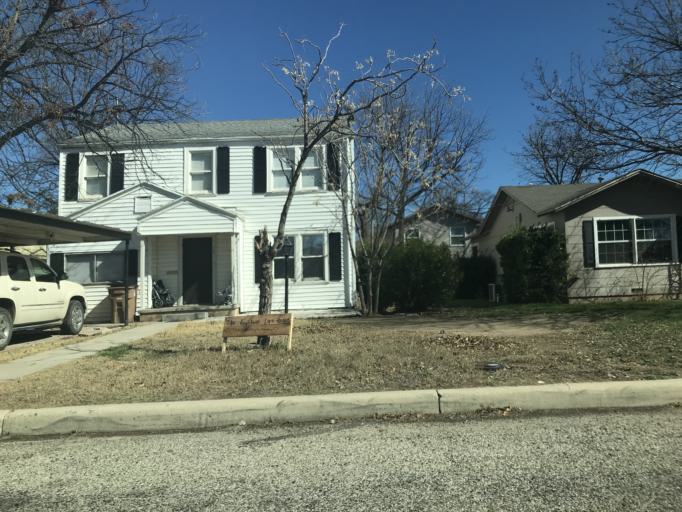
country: US
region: Texas
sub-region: Tom Green County
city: San Angelo
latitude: 31.4514
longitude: -100.4447
